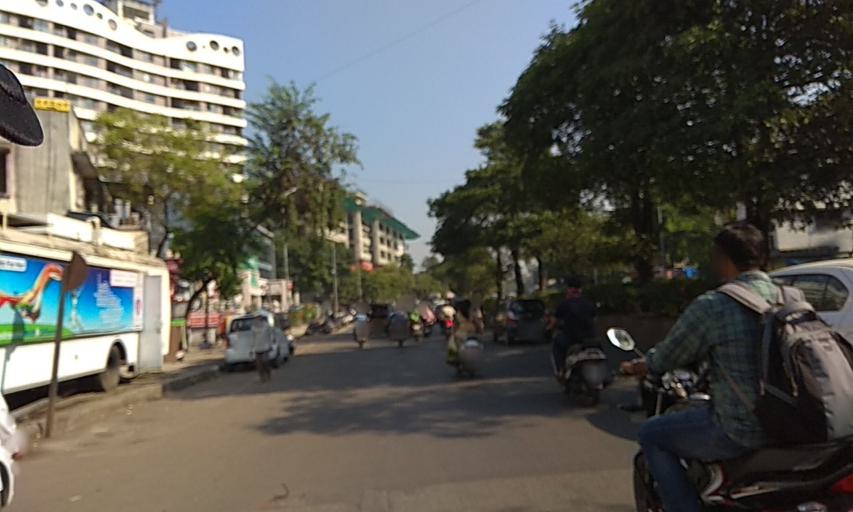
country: IN
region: Maharashtra
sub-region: Pune Division
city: Pune
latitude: 18.4791
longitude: 73.8243
